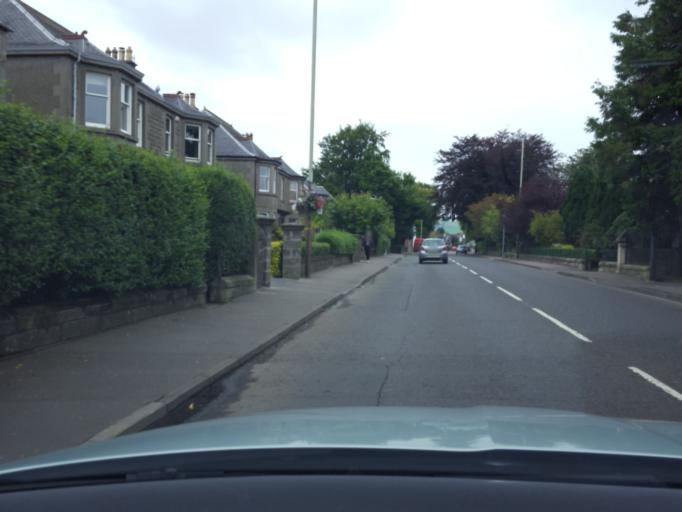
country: GB
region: Scotland
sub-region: Perth and Kinross
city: Kinross
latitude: 56.2117
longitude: -3.4257
